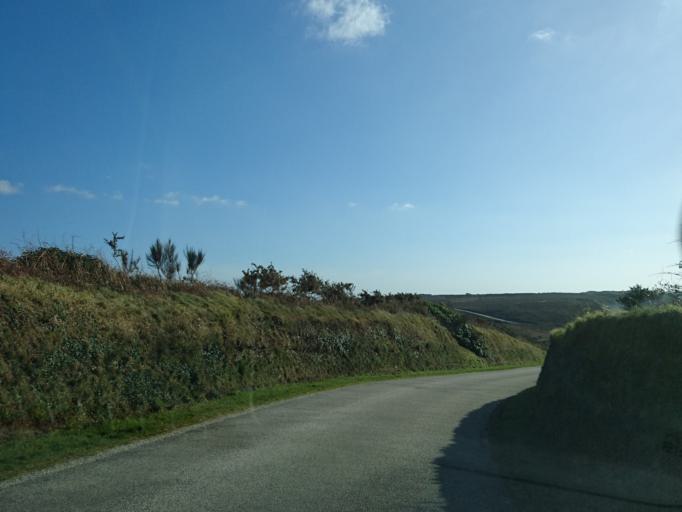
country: FR
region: Brittany
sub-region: Departement du Finistere
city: Roscanvel
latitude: 48.3118
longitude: -4.5703
